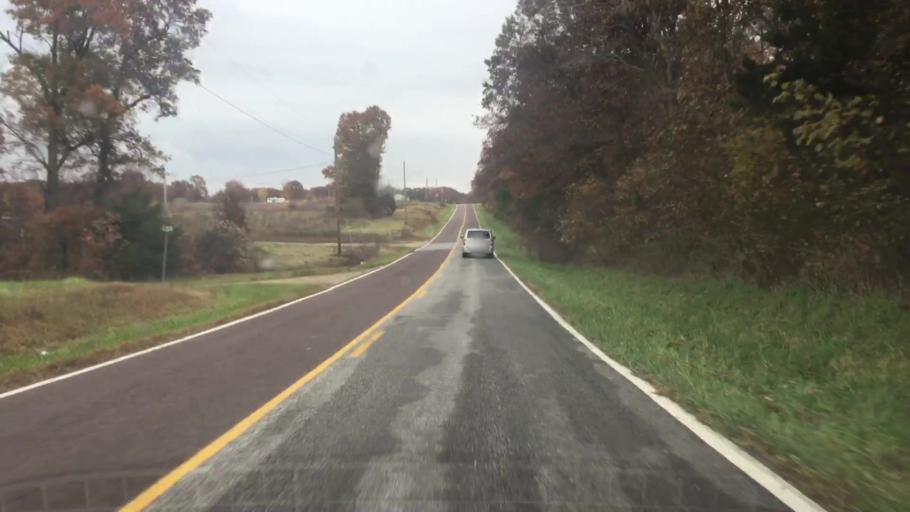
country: US
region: Missouri
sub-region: Callaway County
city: Fulton
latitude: 38.7872
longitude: -91.7686
